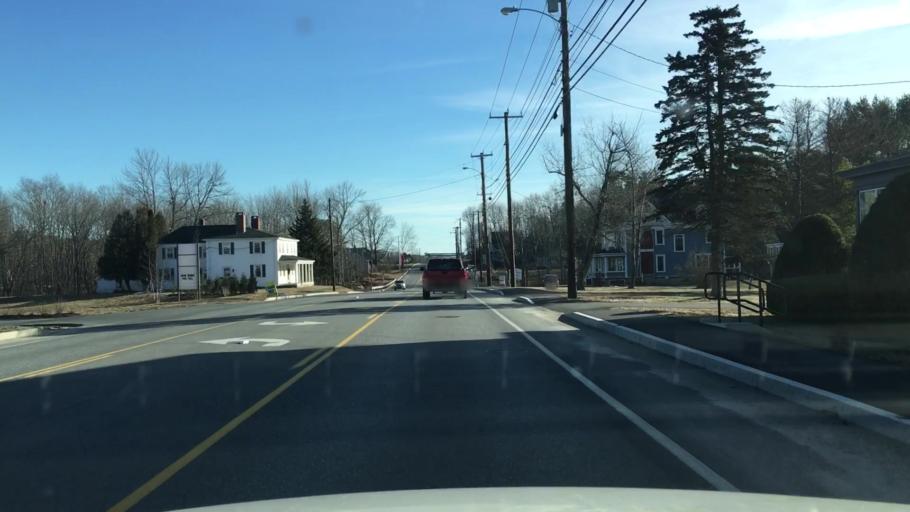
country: US
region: Maine
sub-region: Hancock County
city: Ellsworth
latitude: 44.5585
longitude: -68.4351
